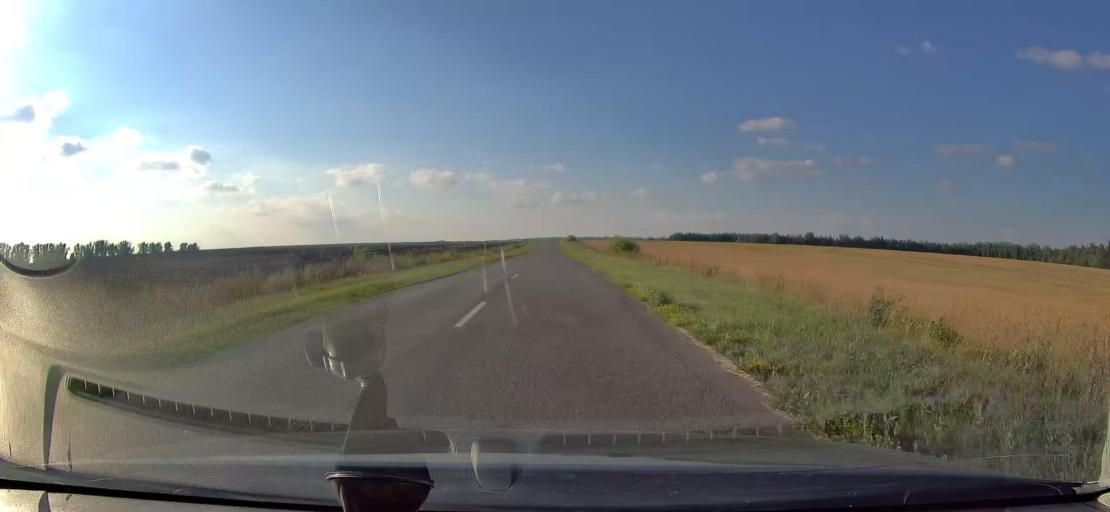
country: RU
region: Kursk
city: Zolotukhino
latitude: 52.0492
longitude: 36.2064
